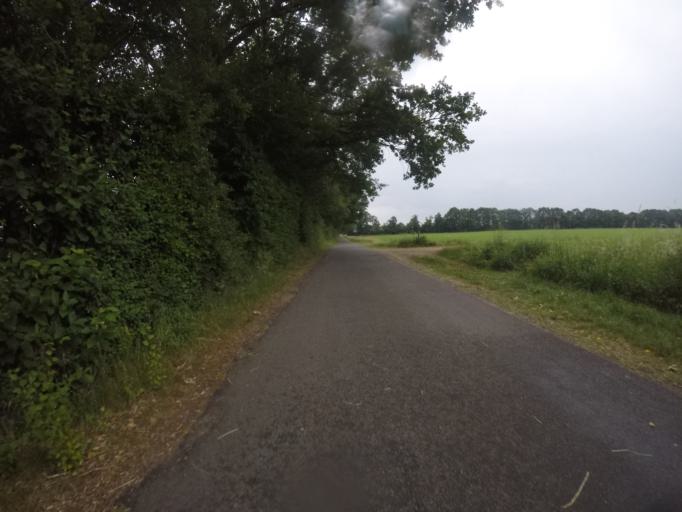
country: DE
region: North Rhine-Westphalia
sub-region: Regierungsbezirk Dusseldorf
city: Bocholt
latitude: 51.8385
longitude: 6.5658
